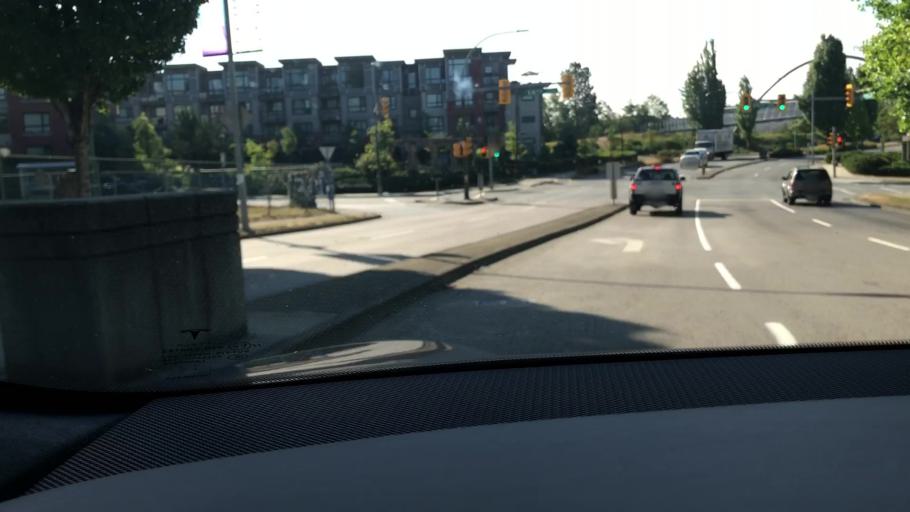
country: CA
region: British Columbia
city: New Westminster
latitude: 49.2102
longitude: -122.9543
